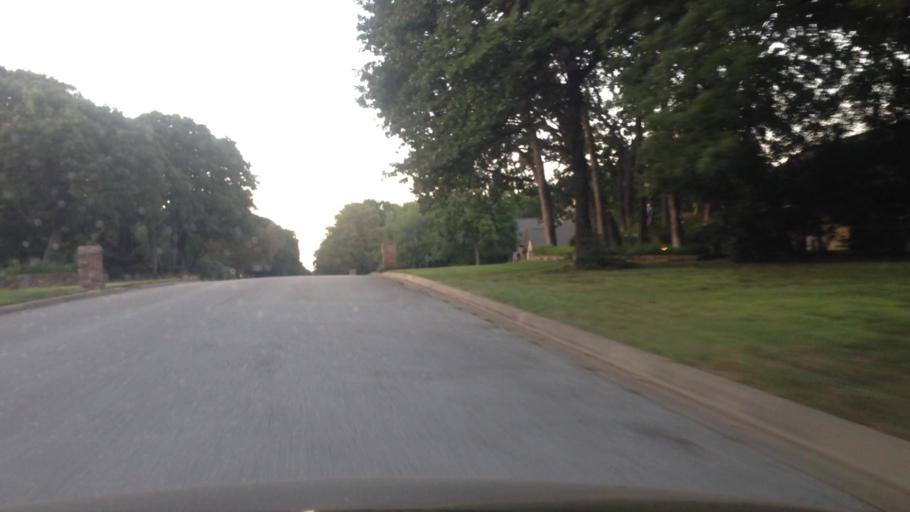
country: US
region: Texas
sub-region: Denton County
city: Trophy Club
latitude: 32.9499
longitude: -97.1987
